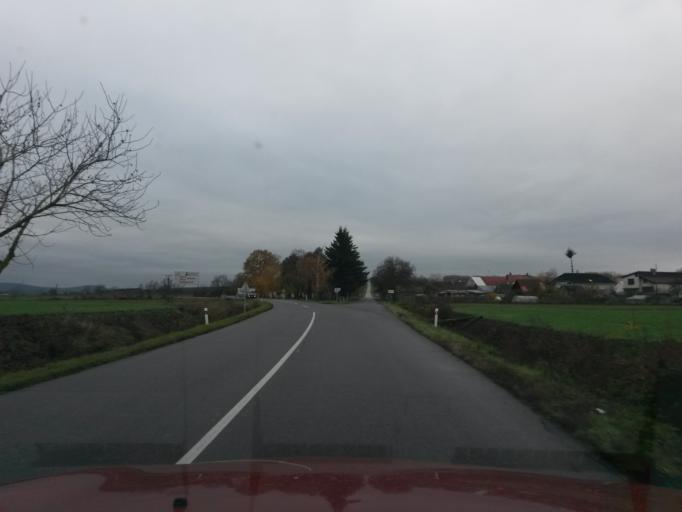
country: SK
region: Kosicky
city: Trebisov
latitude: 48.5796
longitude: 21.6407
